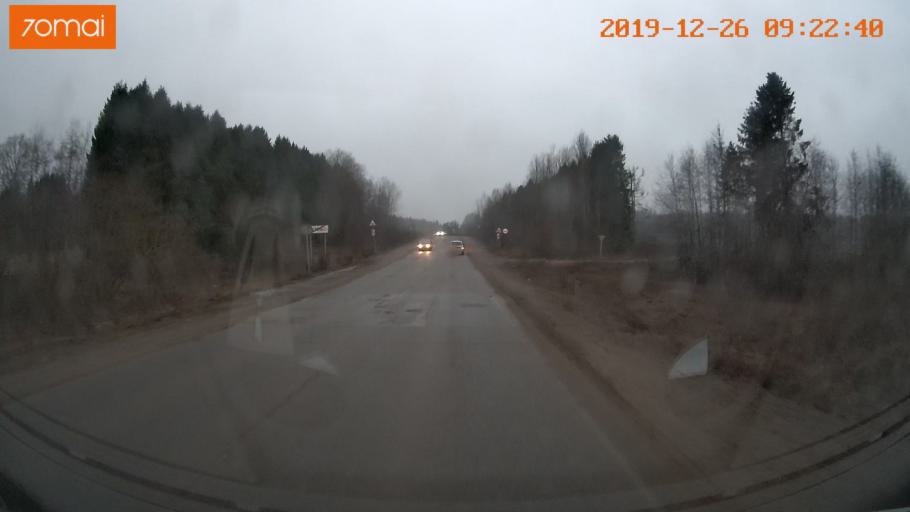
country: RU
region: Vologda
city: Gryazovets
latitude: 58.9831
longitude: 40.2140
